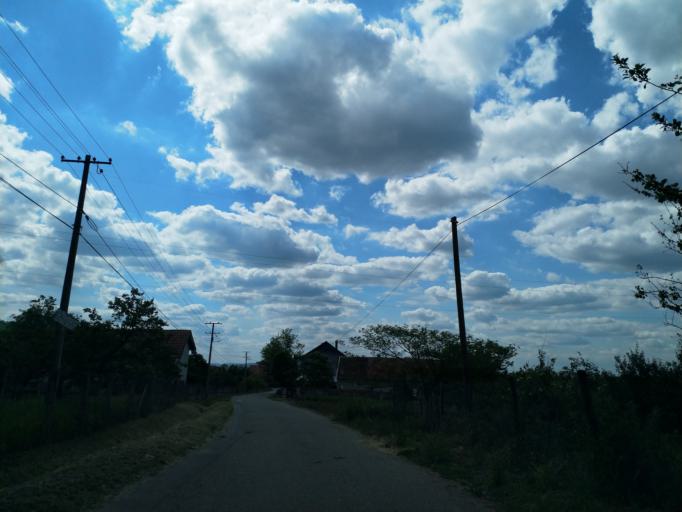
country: RS
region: Central Serbia
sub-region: Pomoravski Okrug
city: Jagodina
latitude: 43.9397
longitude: 21.3097
